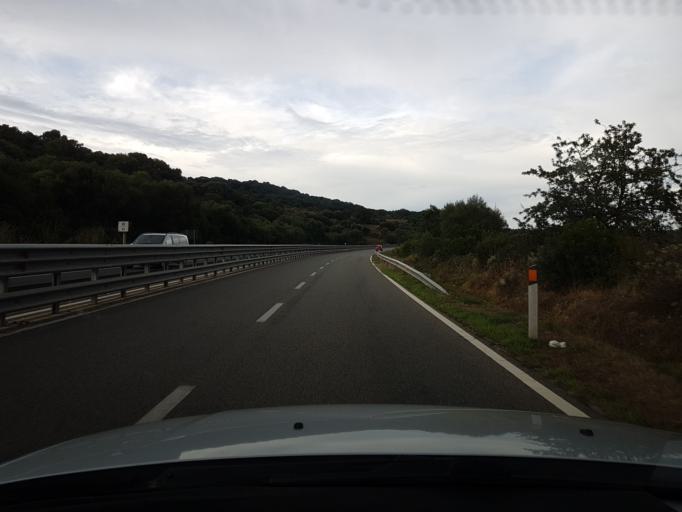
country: IT
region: Sardinia
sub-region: Provincia di Oristano
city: Sedilo
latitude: 40.1564
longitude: 8.9058
